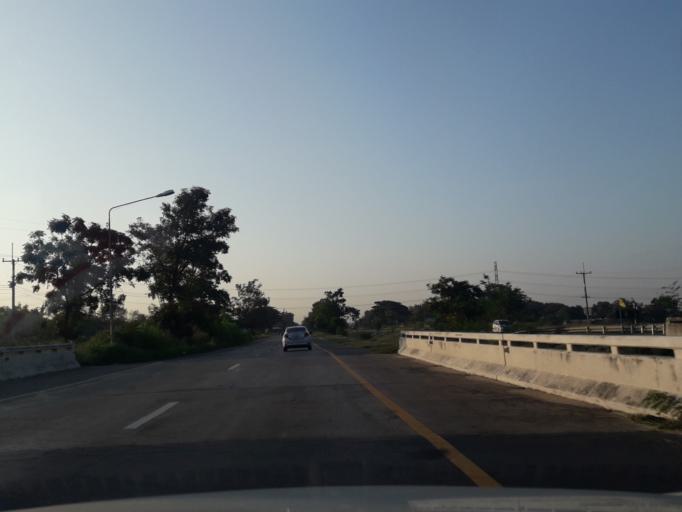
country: TH
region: Phra Nakhon Si Ayutthaya
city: Bang Pa-in
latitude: 14.2769
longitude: 100.5291
